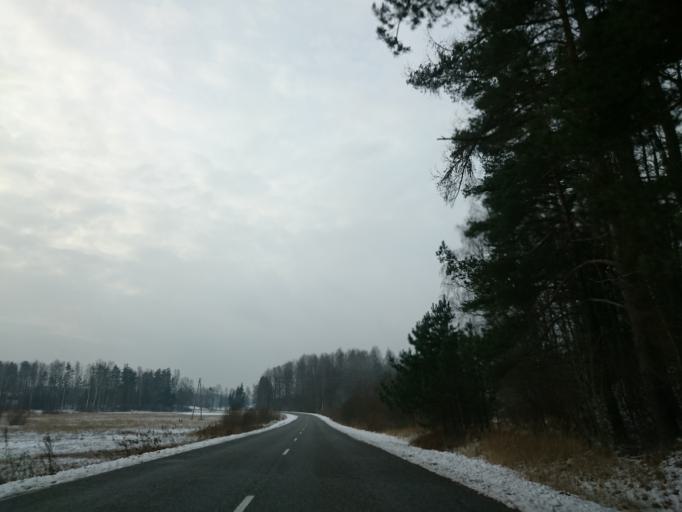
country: LV
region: Seja
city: Loja
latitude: 57.1936
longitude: 24.5988
